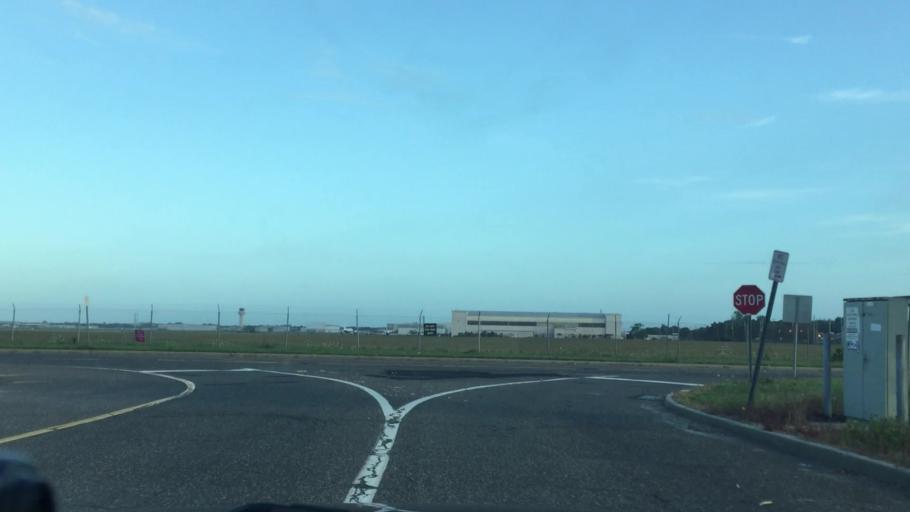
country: US
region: New York
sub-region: Suffolk County
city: Ronkonkoma
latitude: 40.8060
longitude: -73.1094
